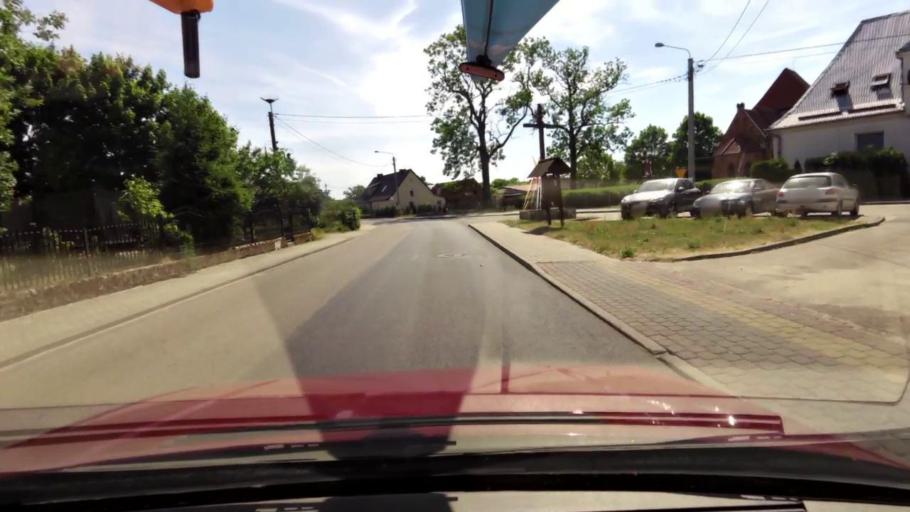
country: PL
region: Pomeranian Voivodeship
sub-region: Powiat slupski
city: Kobylnica
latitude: 54.3890
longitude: 16.9756
